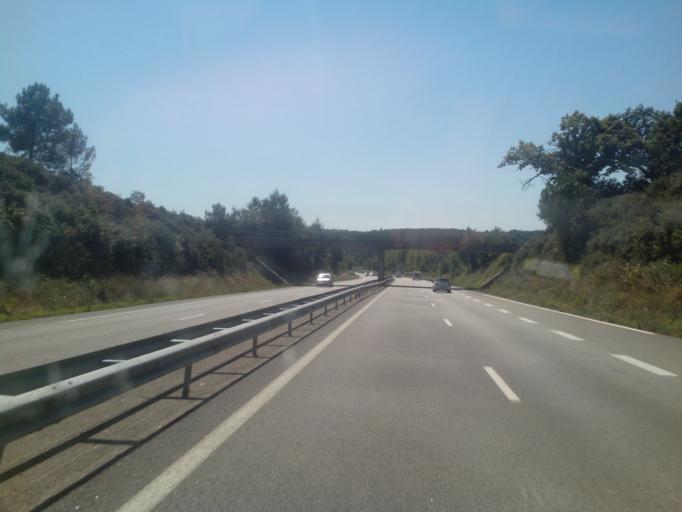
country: FR
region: Brittany
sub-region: Departement du Morbihan
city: Serent
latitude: 47.7973
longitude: -2.4488
